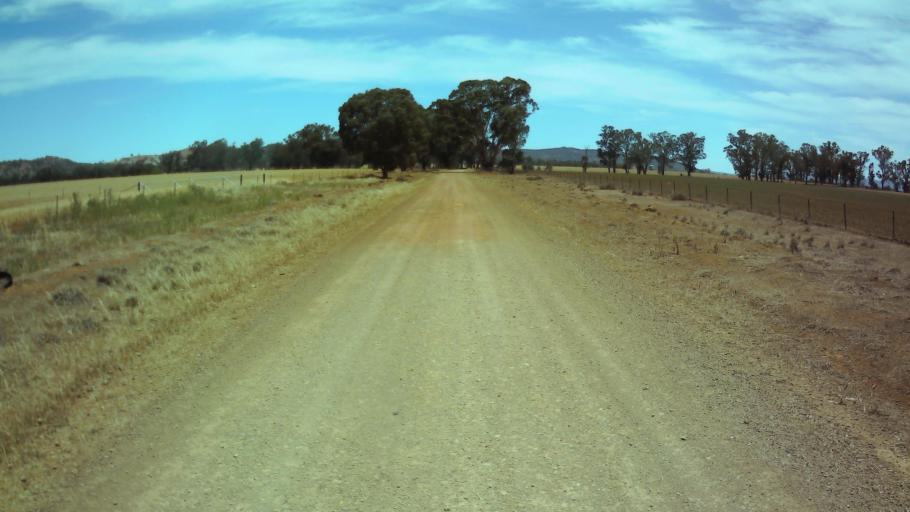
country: AU
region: New South Wales
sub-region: Weddin
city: Grenfell
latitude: -33.7548
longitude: 148.1437
